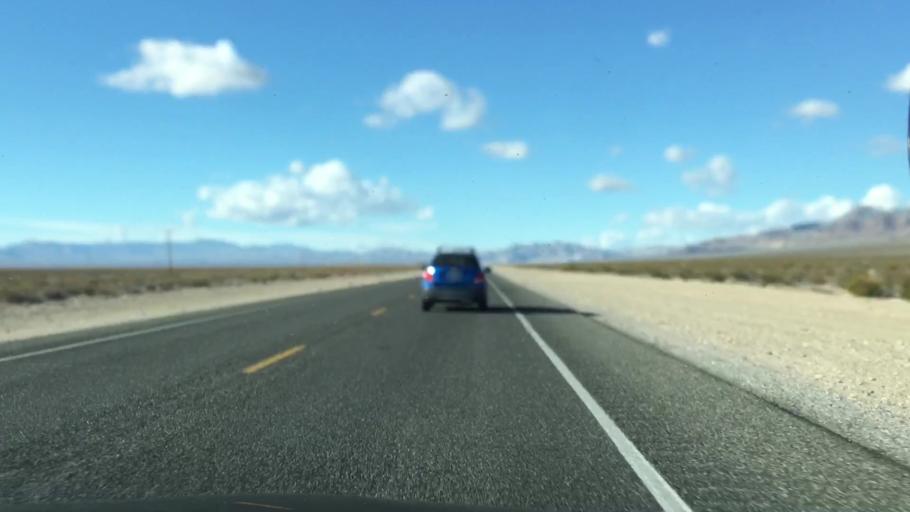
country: US
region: Nevada
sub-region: Nye County
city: Beatty
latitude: 36.7359
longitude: -116.6386
